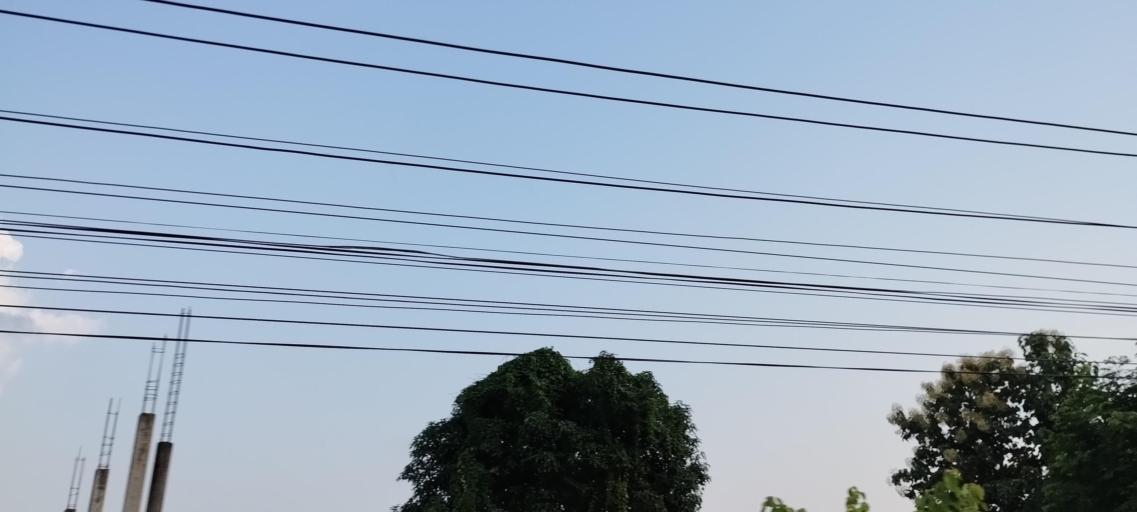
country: NP
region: Far Western
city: Tikapur
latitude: 28.4695
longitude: 81.2759
